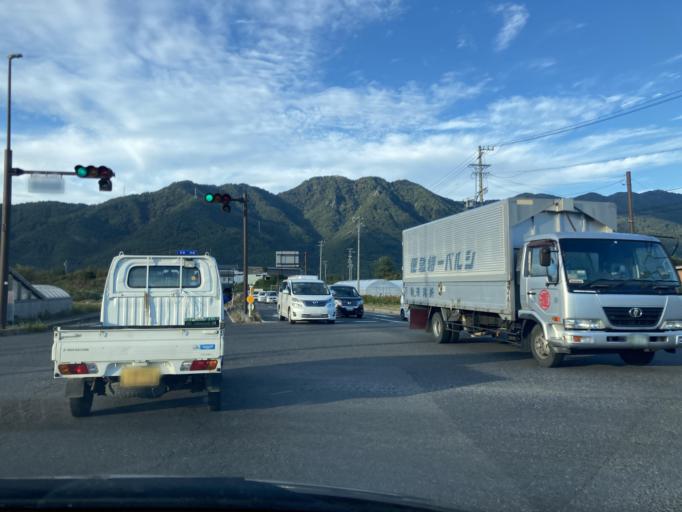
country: JP
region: Nagano
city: Ueda
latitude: 36.4034
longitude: 138.2098
